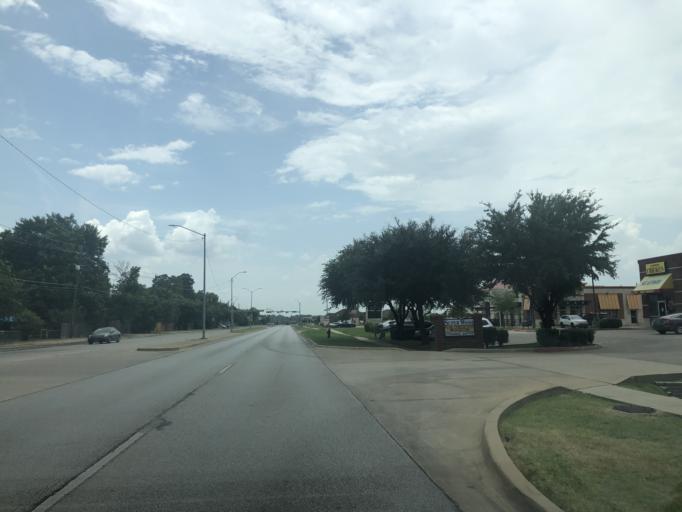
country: US
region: Texas
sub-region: Dallas County
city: Grand Prairie
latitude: 32.7351
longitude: -97.0147
